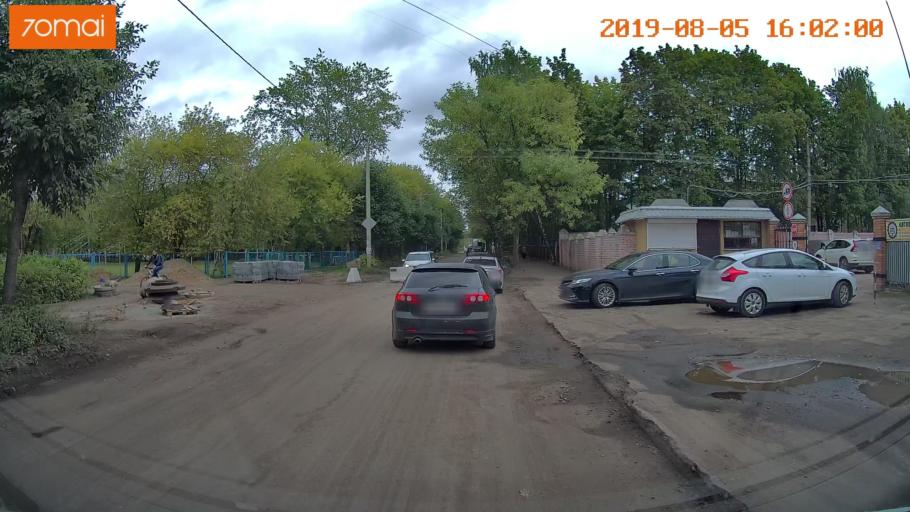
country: RU
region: Ivanovo
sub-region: Gorod Ivanovo
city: Ivanovo
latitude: 56.9772
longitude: 40.9614
